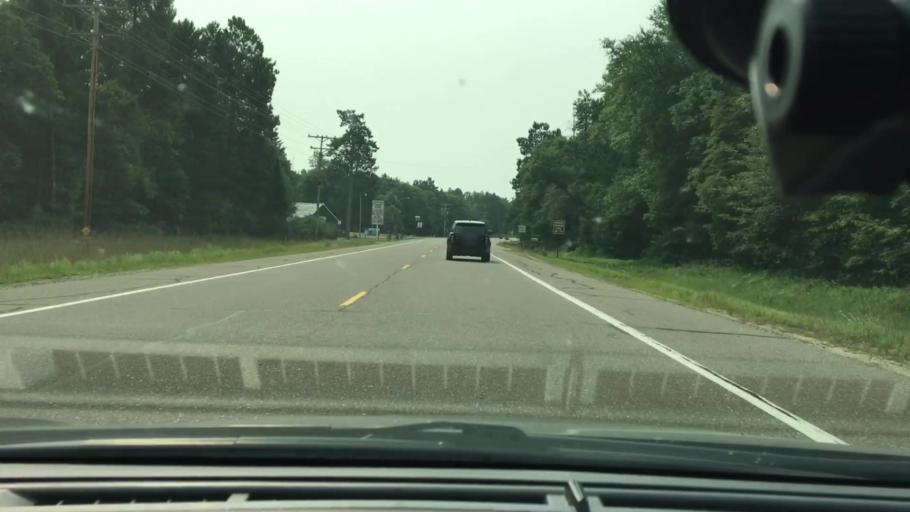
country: US
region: Minnesota
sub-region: Crow Wing County
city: Cross Lake
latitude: 46.5750
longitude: -94.1305
